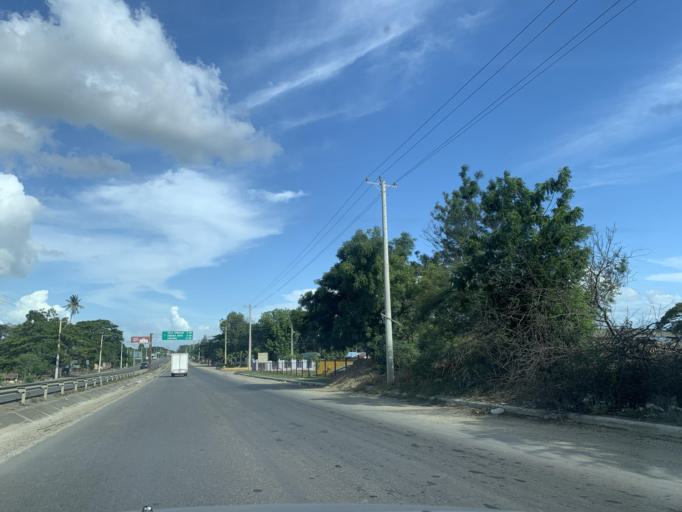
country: DO
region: Santiago
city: Villa Gonzalez
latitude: 19.5494
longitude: -70.8120
